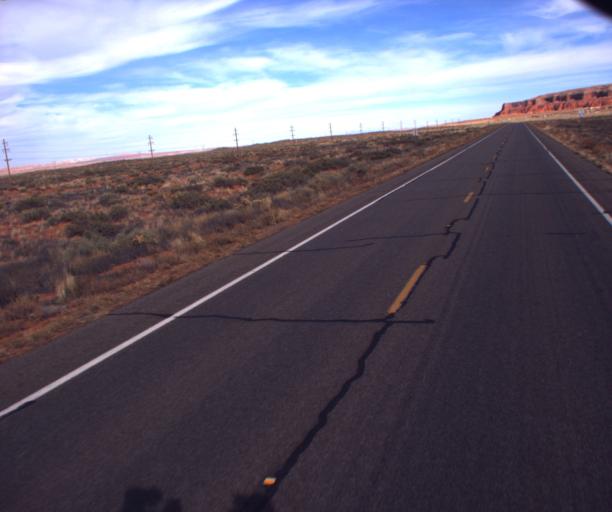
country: US
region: Arizona
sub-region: Navajo County
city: Kayenta
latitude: 36.7842
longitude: -109.9719
